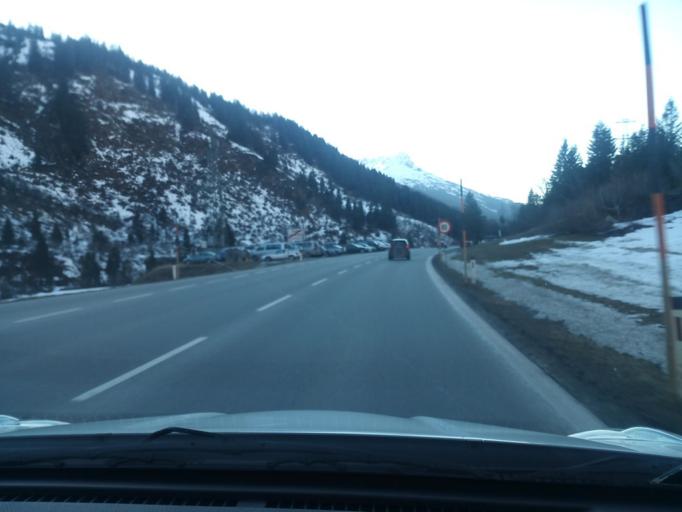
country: AT
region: Vorarlberg
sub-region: Politischer Bezirk Bludenz
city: Lech
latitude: 47.1388
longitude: 10.1564
